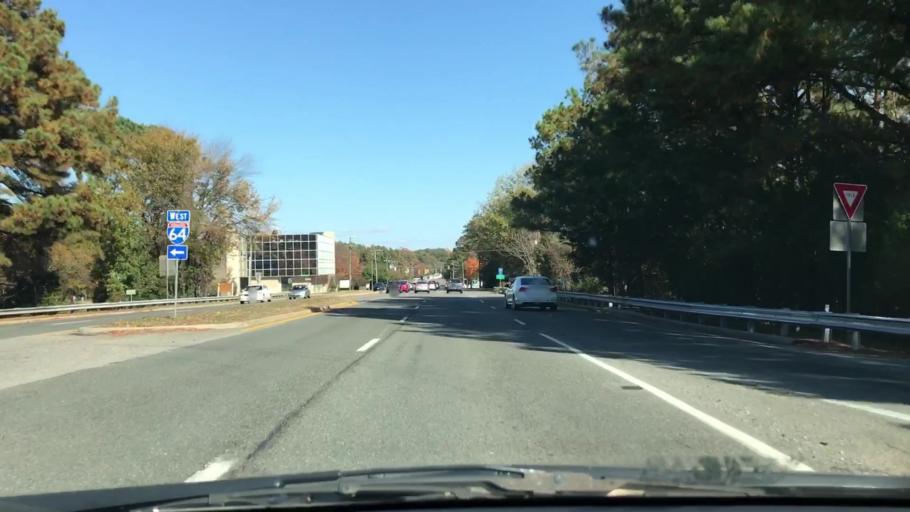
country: US
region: Virginia
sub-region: Henrico County
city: Tuckahoe
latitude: 37.6247
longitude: -77.5529
